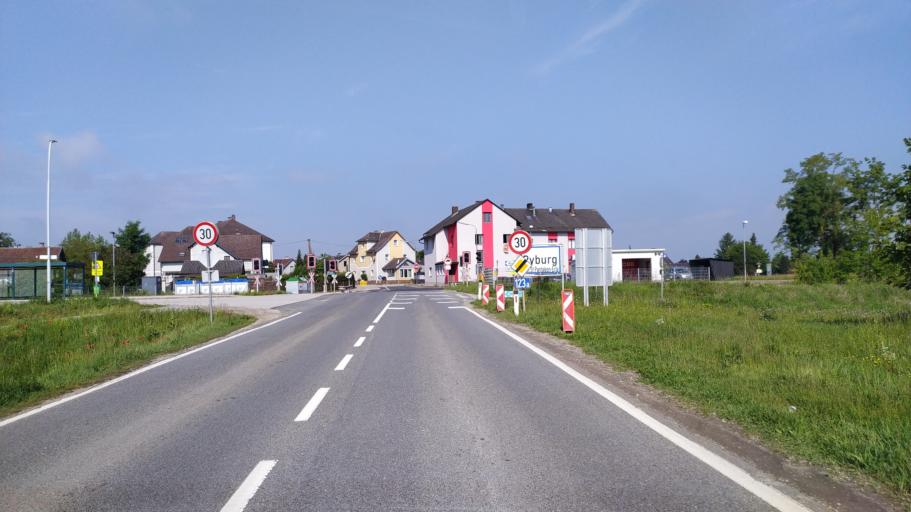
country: AT
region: Lower Austria
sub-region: Politischer Bezirk Amstetten
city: Ennsdorf
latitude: 48.2274
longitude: 14.5293
